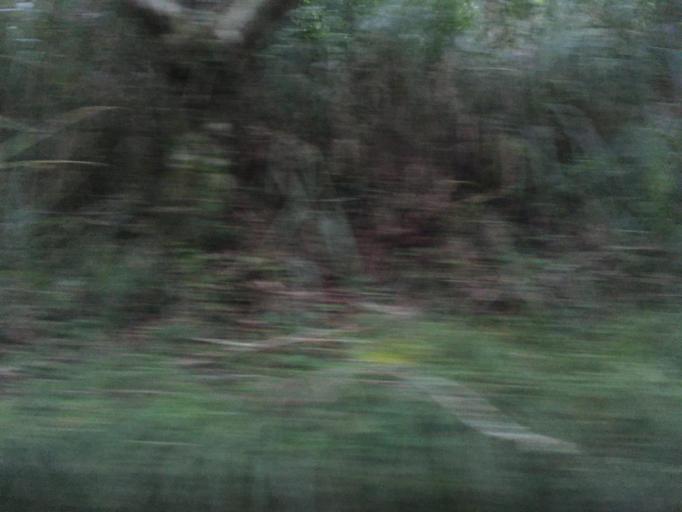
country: TW
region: Taiwan
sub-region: Yilan
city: Yilan
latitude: 24.5143
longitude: 121.5887
